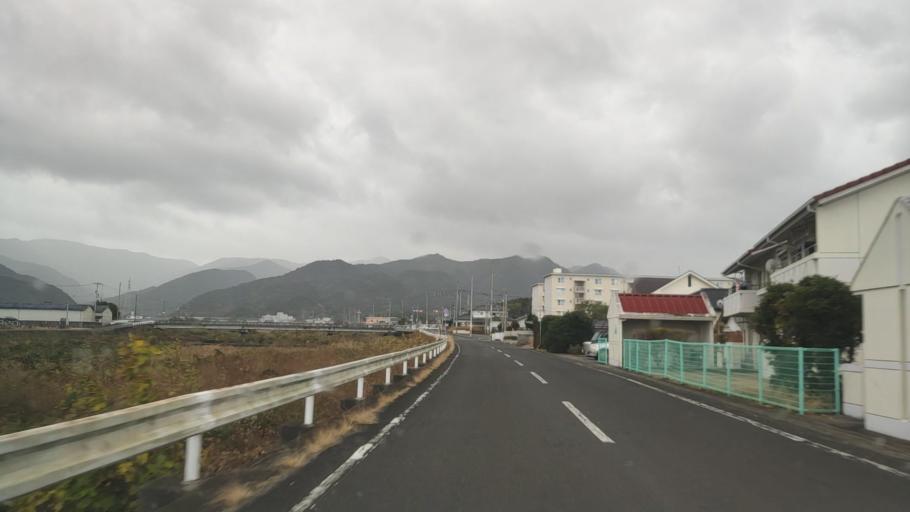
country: JP
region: Tokushima
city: Ishii
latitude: 34.2183
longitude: 134.4091
